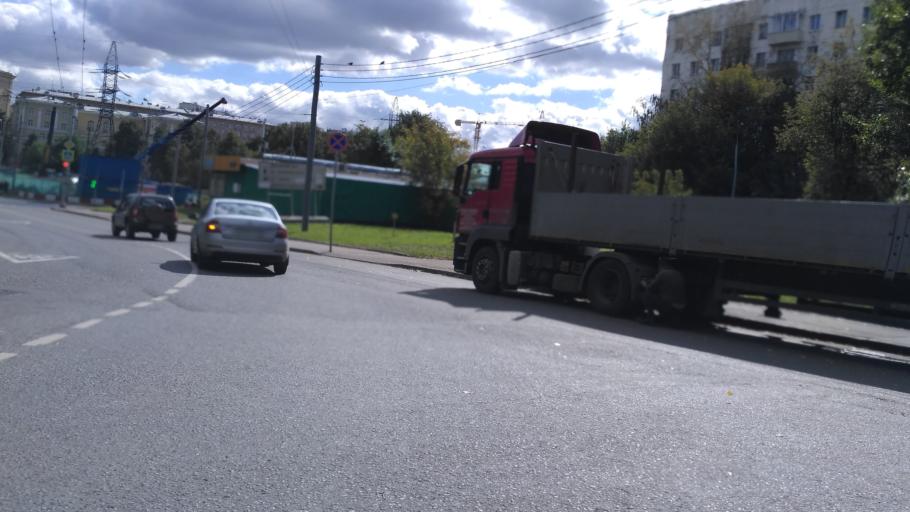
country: RU
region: Moscow
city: Ostankinskiy
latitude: 55.8167
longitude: 37.6305
